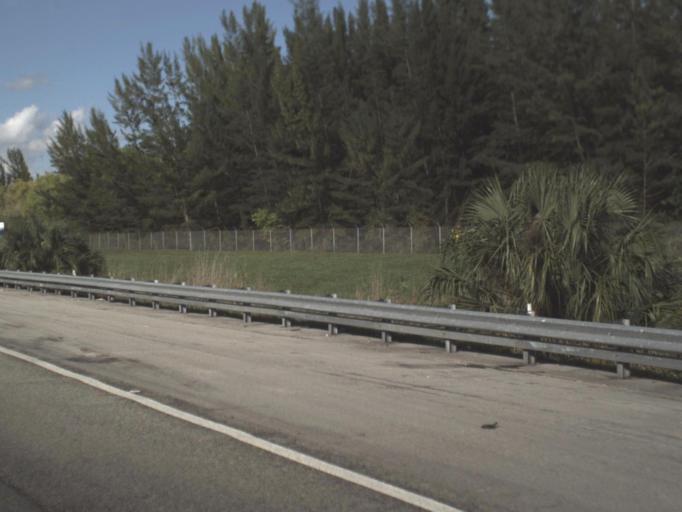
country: US
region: Florida
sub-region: Broward County
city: Coconut Creek
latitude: 26.2667
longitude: -80.1686
